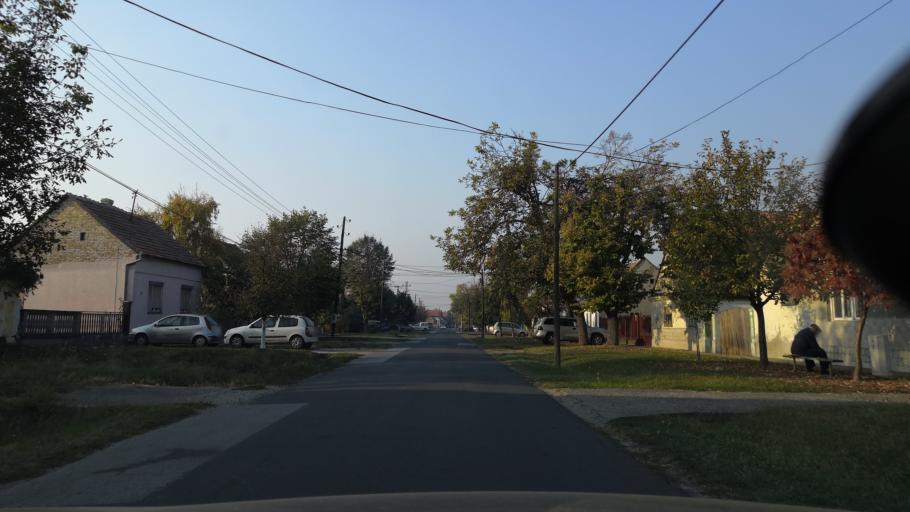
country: RS
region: Autonomna Pokrajina Vojvodina
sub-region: Sremski Okrug
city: Stara Pazova
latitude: 44.9932
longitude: 20.1470
